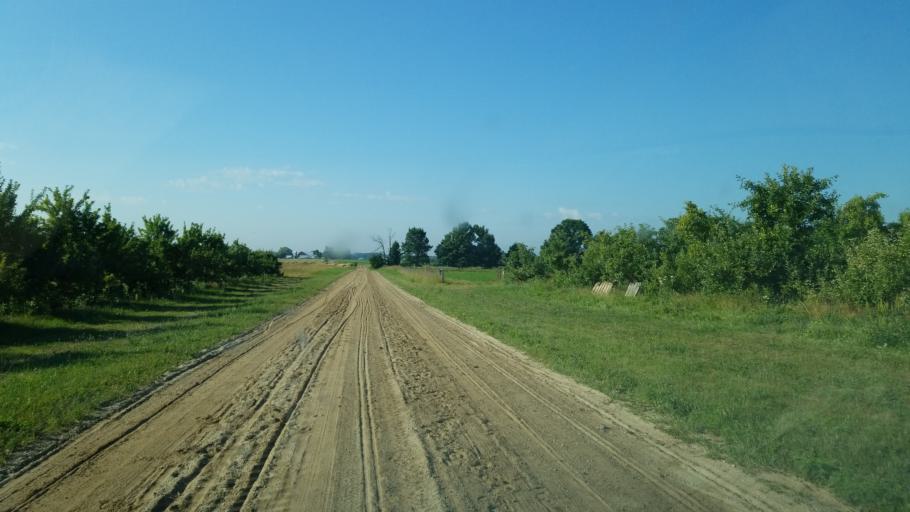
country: US
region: Michigan
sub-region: Mecosta County
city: Canadian Lakes
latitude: 43.5605
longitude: -85.3537
